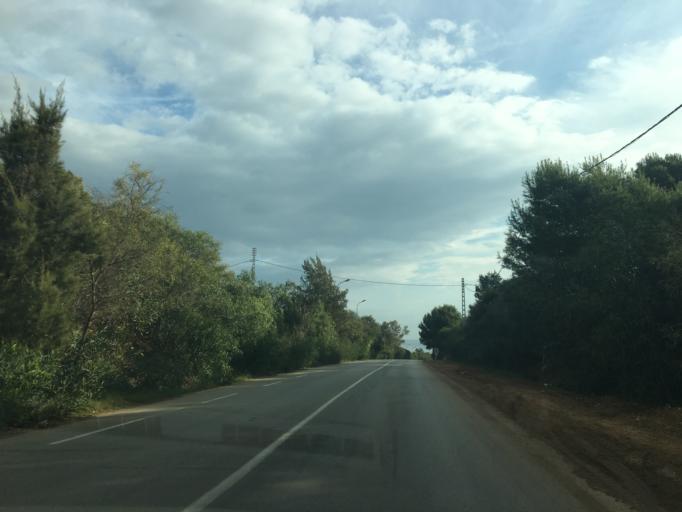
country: DZ
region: Tipaza
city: Tipasa
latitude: 36.5890
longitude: 2.4776
